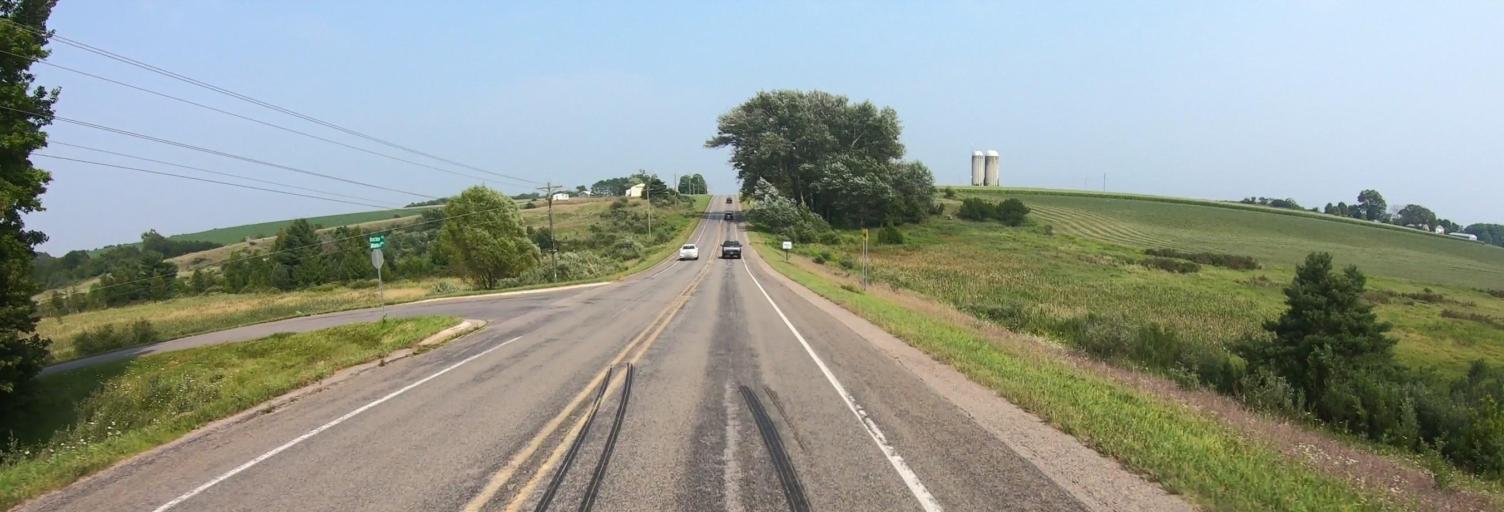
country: US
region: Michigan
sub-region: Charlevoix County
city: Charlevoix
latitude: 45.1850
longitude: -85.3036
